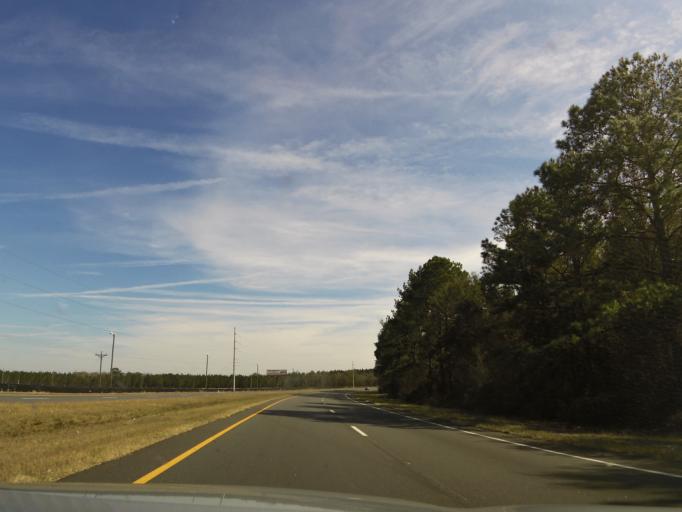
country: US
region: Georgia
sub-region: Brantley County
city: Nahunta
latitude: 31.2331
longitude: -81.7504
